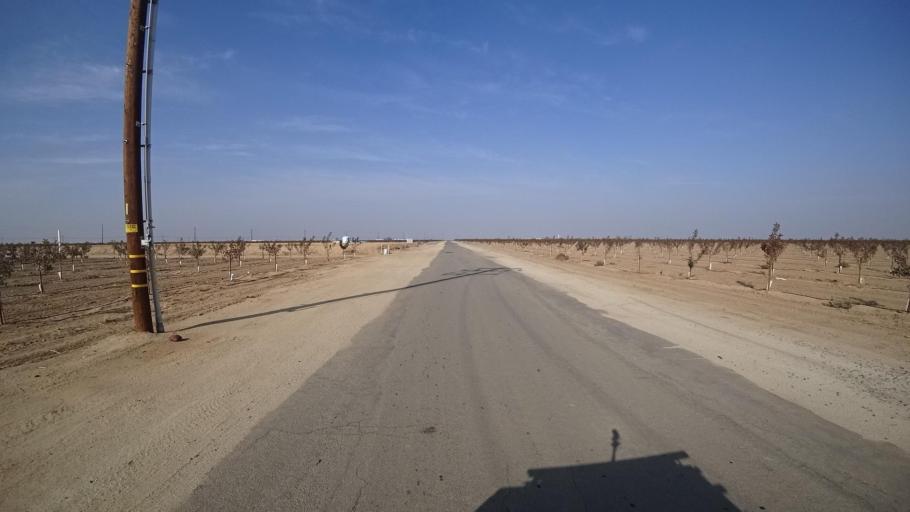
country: US
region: California
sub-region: Tulare County
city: Richgrove
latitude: 35.7808
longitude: -119.1164
